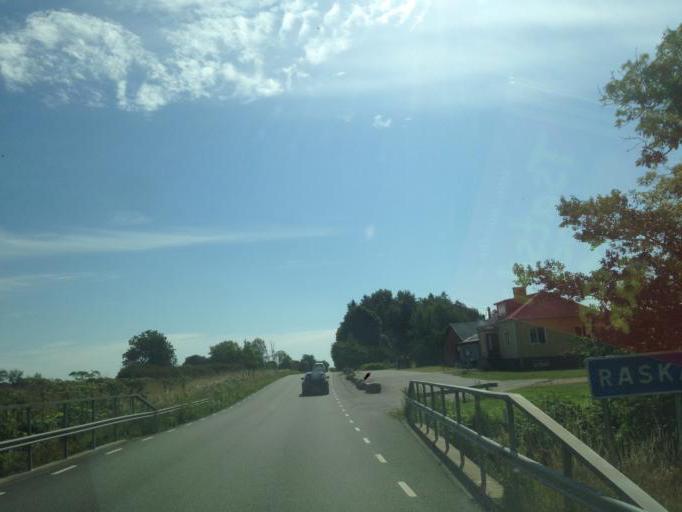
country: SE
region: Skane
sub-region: Simrishamns Kommun
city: Kivik
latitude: 55.6365
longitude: 14.1486
